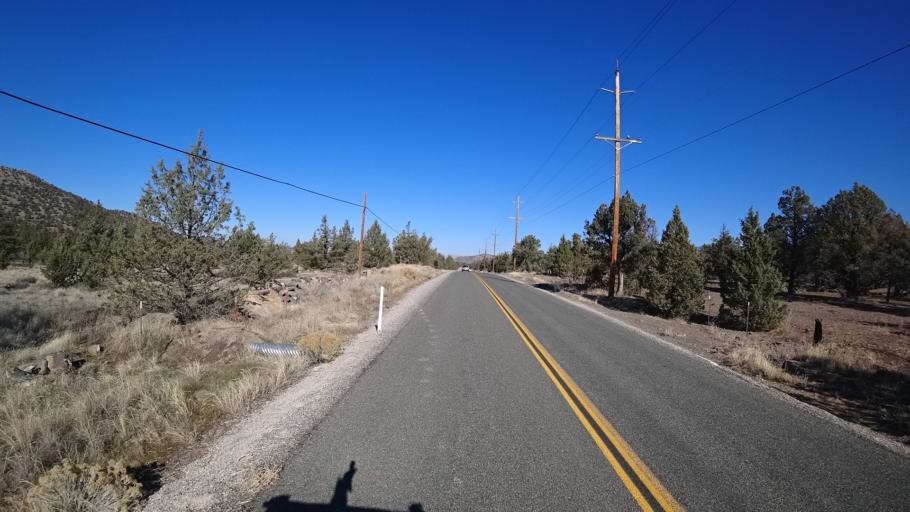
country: US
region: California
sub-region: Siskiyou County
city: Montague
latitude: 41.6647
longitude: -122.3692
